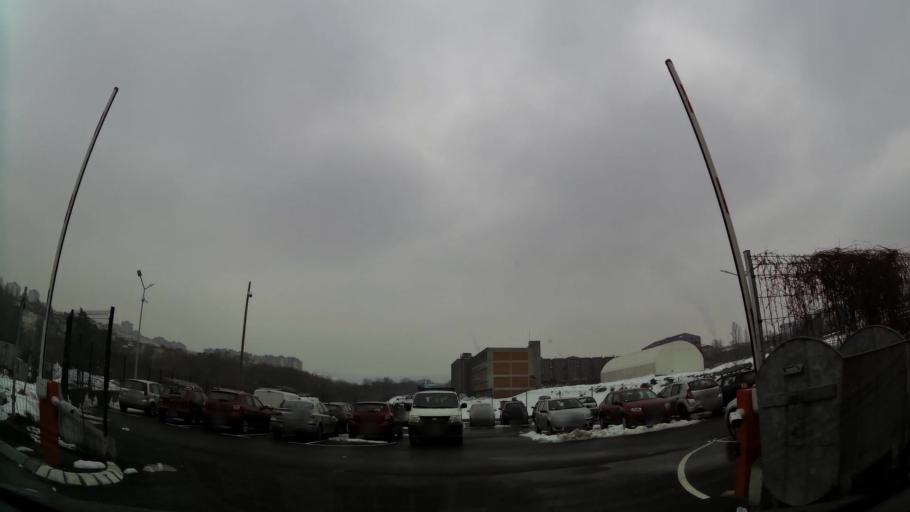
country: RS
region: Central Serbia
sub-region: Belgrade
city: Vozdovac
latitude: 44.7680
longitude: 20.4872
